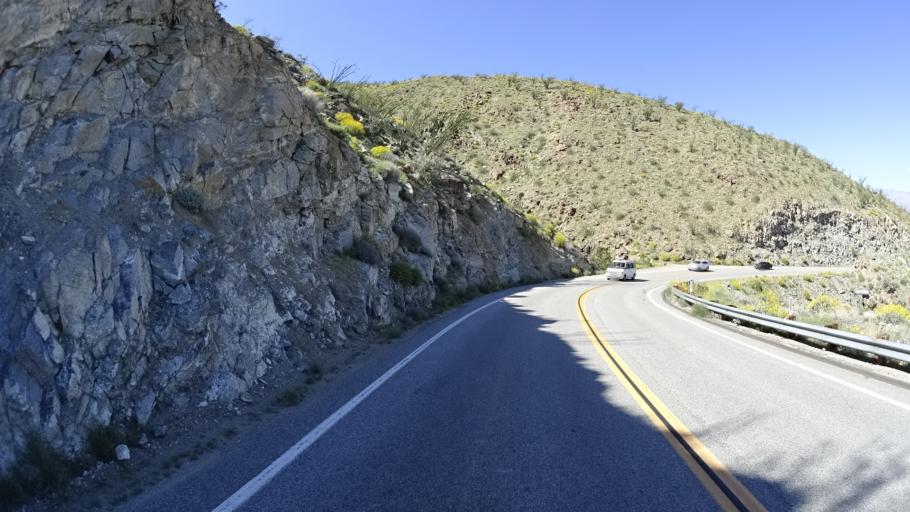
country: US
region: California
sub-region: San Diego County
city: Borrego Springs
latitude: 33.2306
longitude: -116.4116
